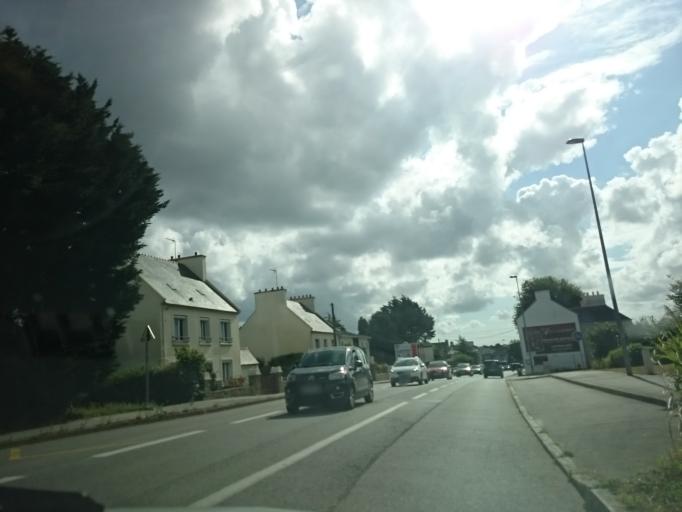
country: FR
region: Brittany
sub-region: Departement du Finistere
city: Le Relecq-Kerhuon
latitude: 48.4146
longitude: -4.4384
